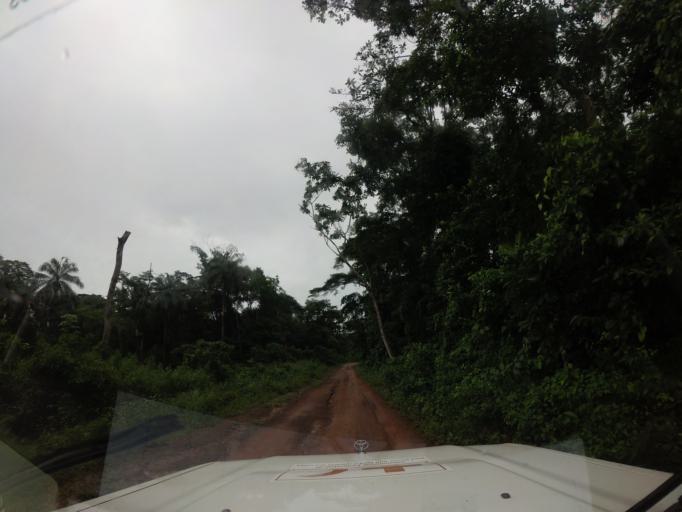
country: SL
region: Eastern Province
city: Kenema
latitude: 7.7212
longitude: -11.1886
